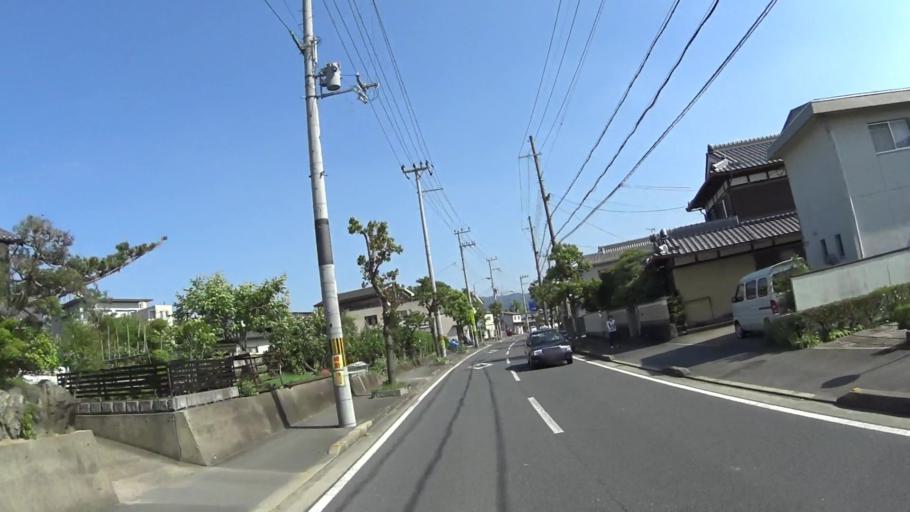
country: JP
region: Kyoto
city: Kameoka
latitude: 35.0239
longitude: 135.5885
